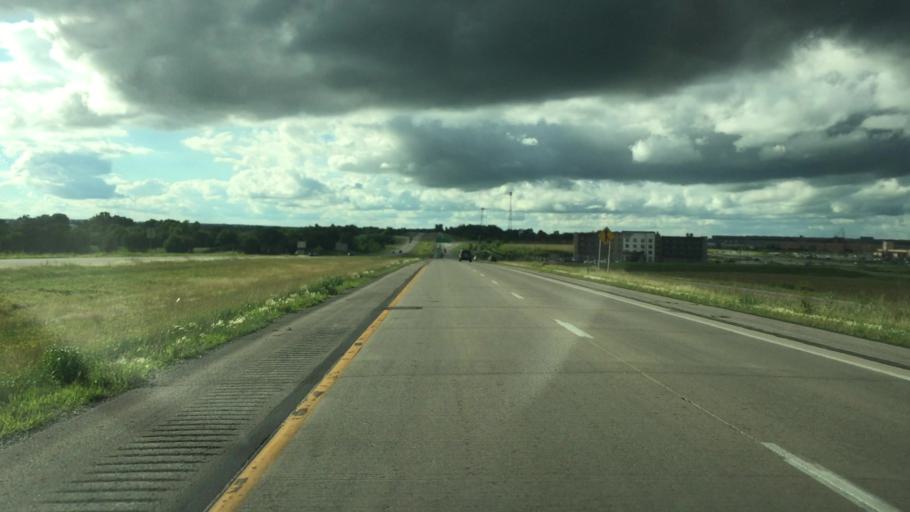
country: US
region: Iowa
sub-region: Polk County
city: Altoona
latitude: 41.6490
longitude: -93.5136
